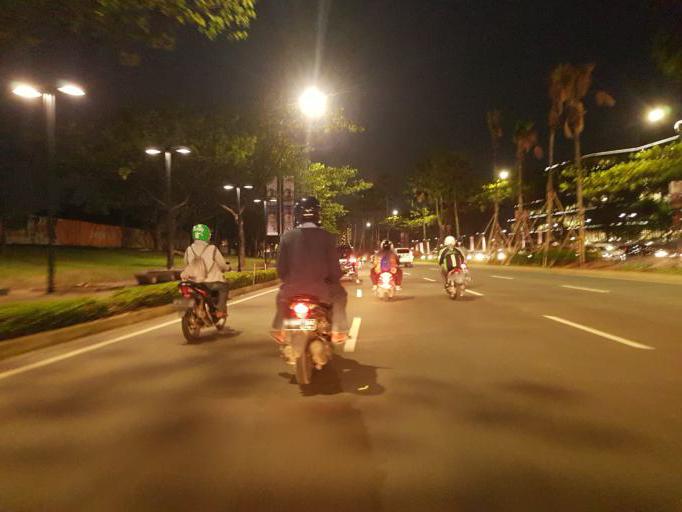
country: ID
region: West Java
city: Serpong
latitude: -6.2999
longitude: 106.6487
